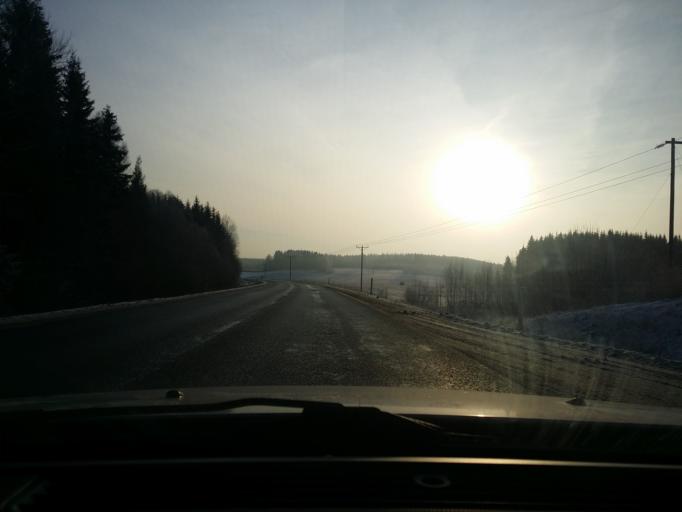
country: SE
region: OErebro
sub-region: Lindesbergs Kommun
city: Lindesberg
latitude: 59.5923
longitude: 15.1853
